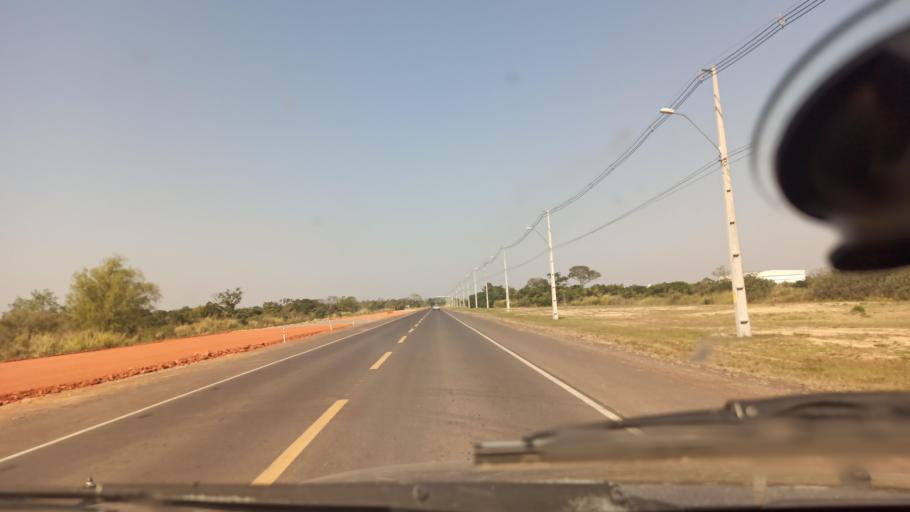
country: PY
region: Central
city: Colonia Mariano Roque Alonso
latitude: -25.1908
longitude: -57.5787
